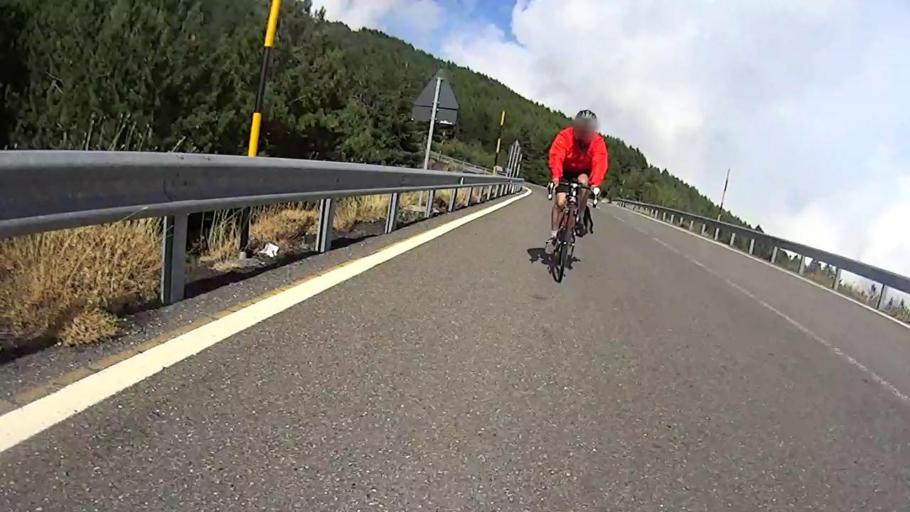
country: IT
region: Sicily
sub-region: Catania
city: Nicolosi
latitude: 37.7006
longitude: 15.0135
